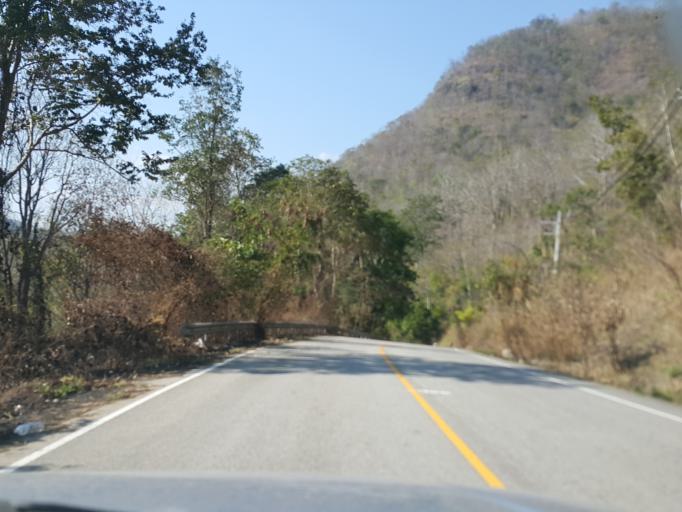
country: TH
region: Chiang Mai
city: Mae Wang
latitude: 18.6204
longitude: 98.7250
